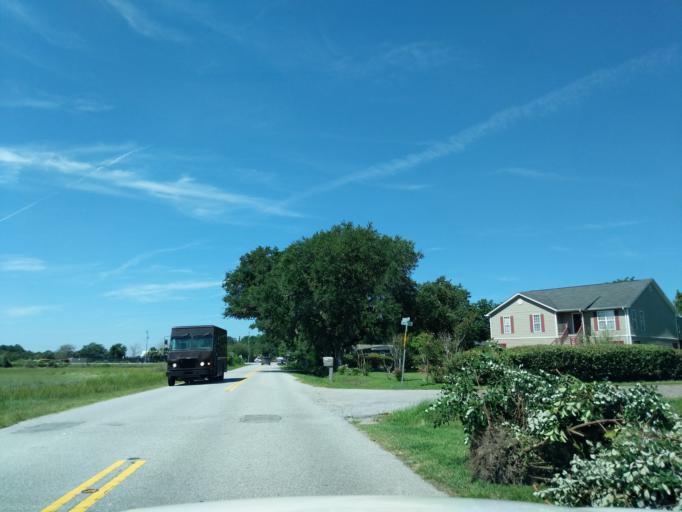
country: US
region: South Carolina
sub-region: Charleston County
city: Folly Beach
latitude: 32.6925
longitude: -79.9621
